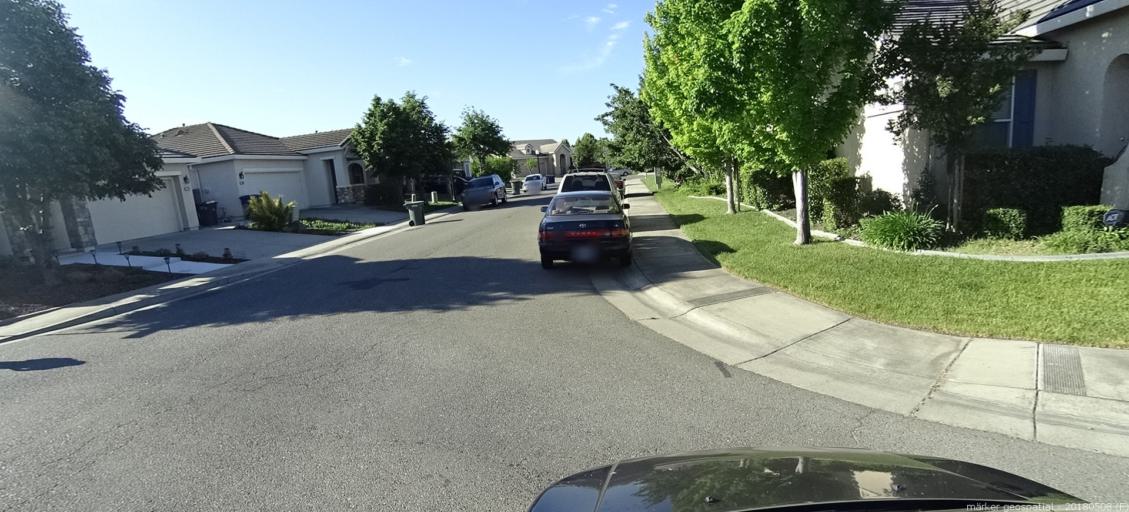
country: US
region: California
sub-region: Sacramento County
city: Elverta
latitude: 38.6834
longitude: -121.5009
